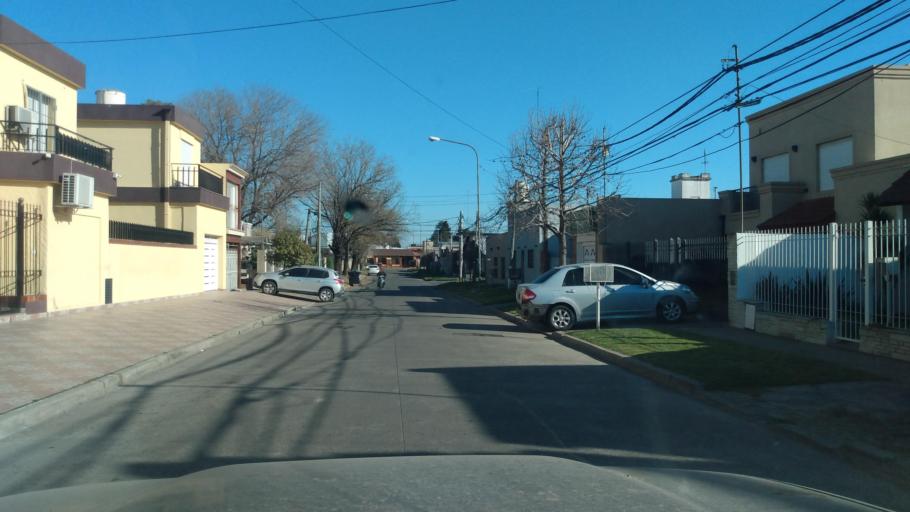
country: AR
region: Buenos Aires
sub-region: Partido de Lujan
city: Lujan
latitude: -34.5619
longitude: -59.0999
